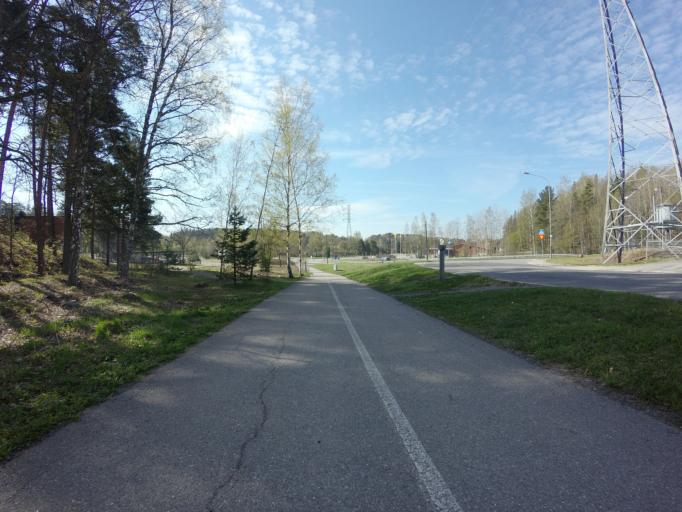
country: FI
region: Varsinais-Suomi
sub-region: Turku
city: Raisio
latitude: 60.4542
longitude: 22.1571
